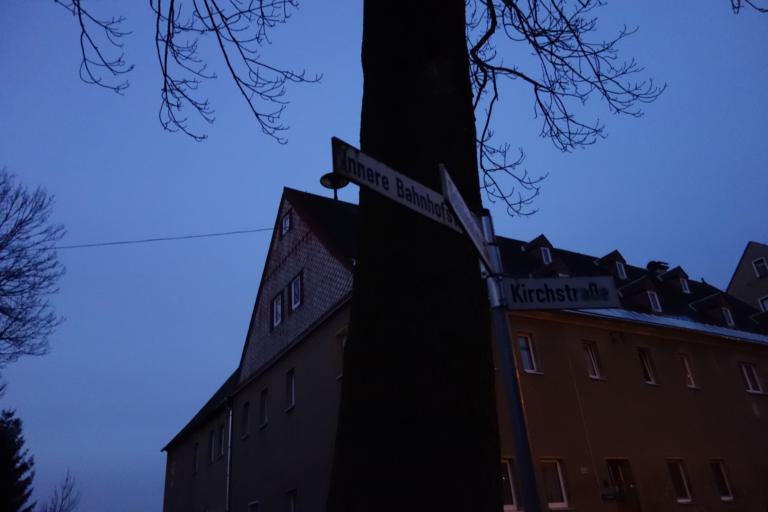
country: DE
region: Saxony
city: Johstadt
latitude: 50.5112
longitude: 13.0957
